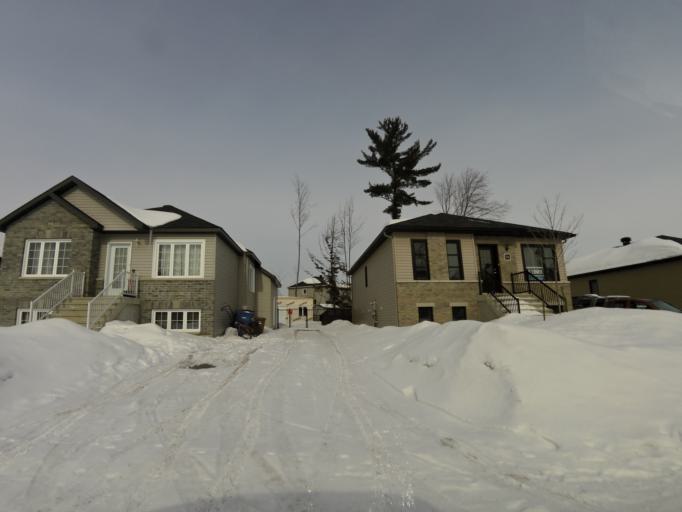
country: CA
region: Quebec
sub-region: Outaouais
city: Gatineau
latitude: 45.5076
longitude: -75.5730
